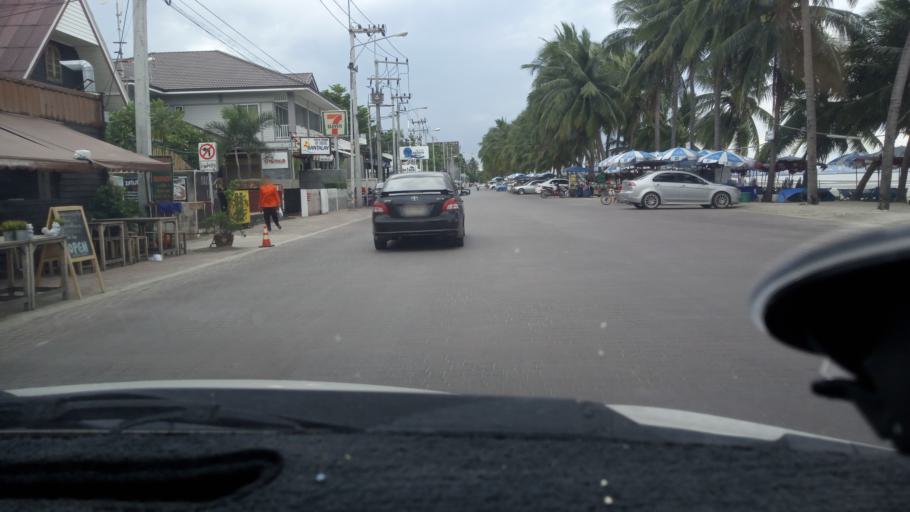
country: TH
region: Chon Buri
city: Chon Buri
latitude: 13.2801
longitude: 100.9177
